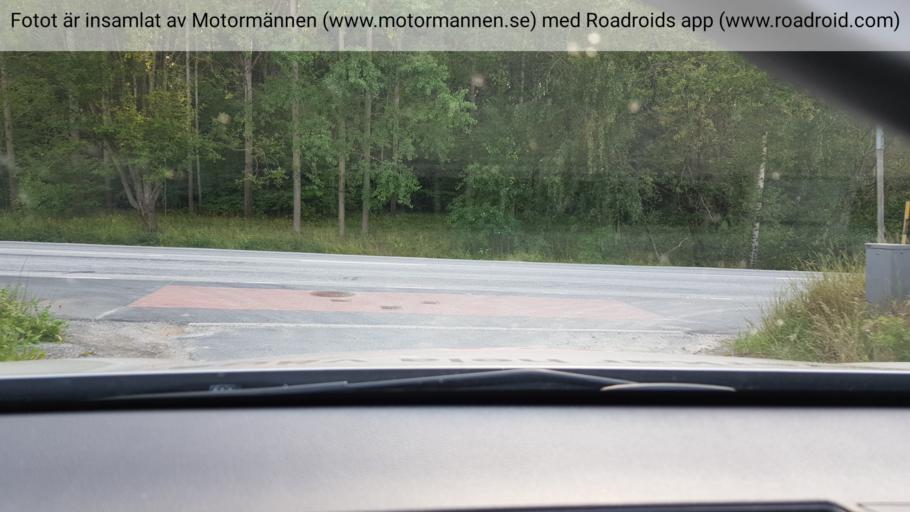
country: SE
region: Stockholm
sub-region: Huddinge Kommun
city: Huddinge
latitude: 59.2247
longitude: 18.0069
